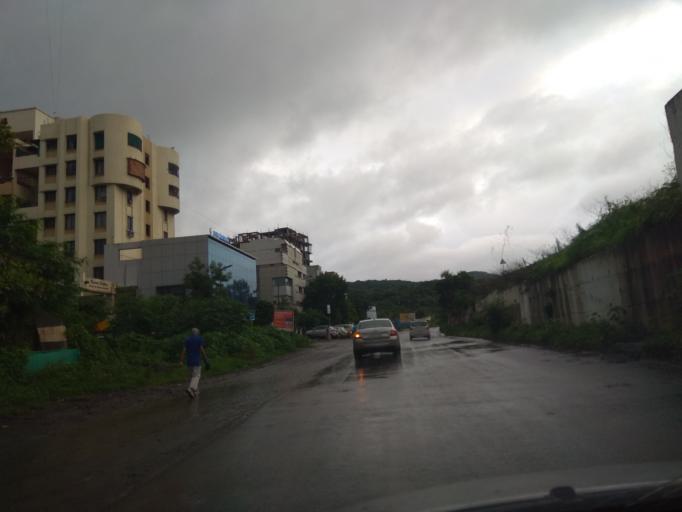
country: IN
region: Maharashtra
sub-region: Pune Division
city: Kharakvasla
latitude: 18.4922
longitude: 73.7890
